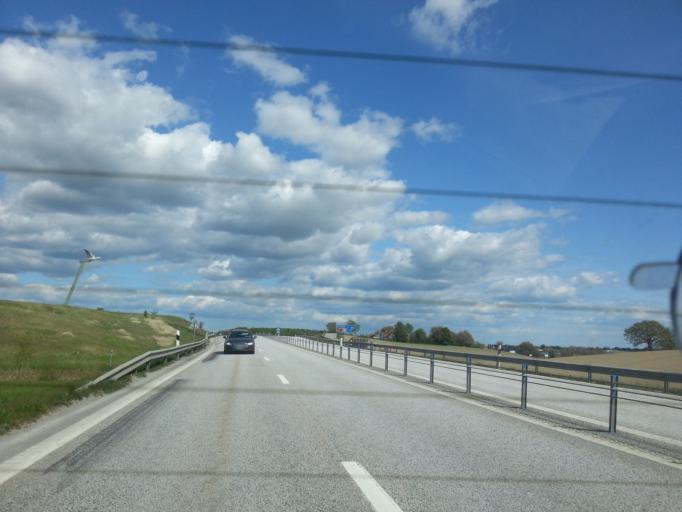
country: SE
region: Skane
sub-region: Skurups Kommun
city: Skurup
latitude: 55.4919
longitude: 13.4737
